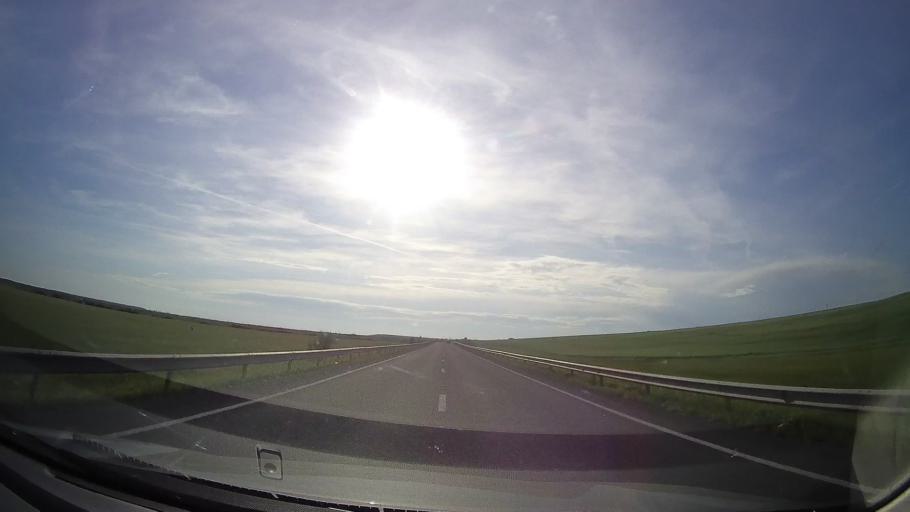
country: RO
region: Timis
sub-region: Comuna Topolovatu Mare
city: Topolovatu Mare
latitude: 45.7912
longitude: 21.5709
